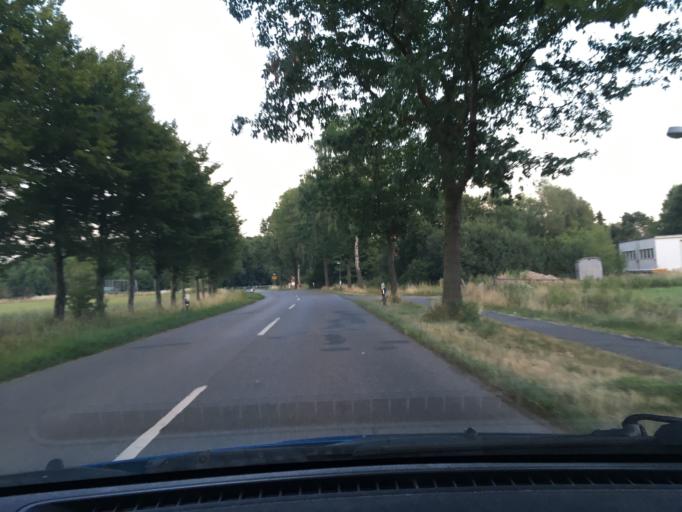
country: DE
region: Lower Saxony
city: Bienenbuttel
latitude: 53.1405
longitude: 10.4984
